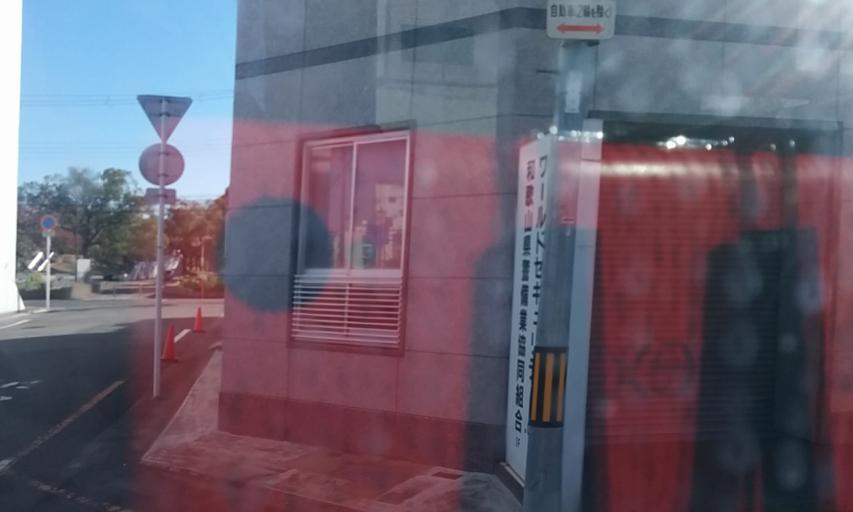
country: JP
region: Wakayama
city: Wakayama-shi
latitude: 34.2361
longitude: 135.1745
